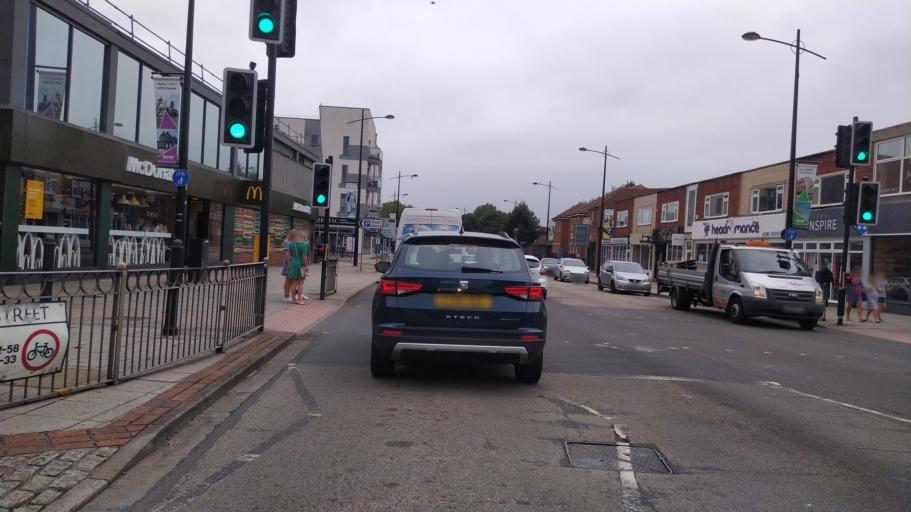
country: GB
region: England
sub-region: Hampshire
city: Havant
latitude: 50.8518
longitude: -0.9846
